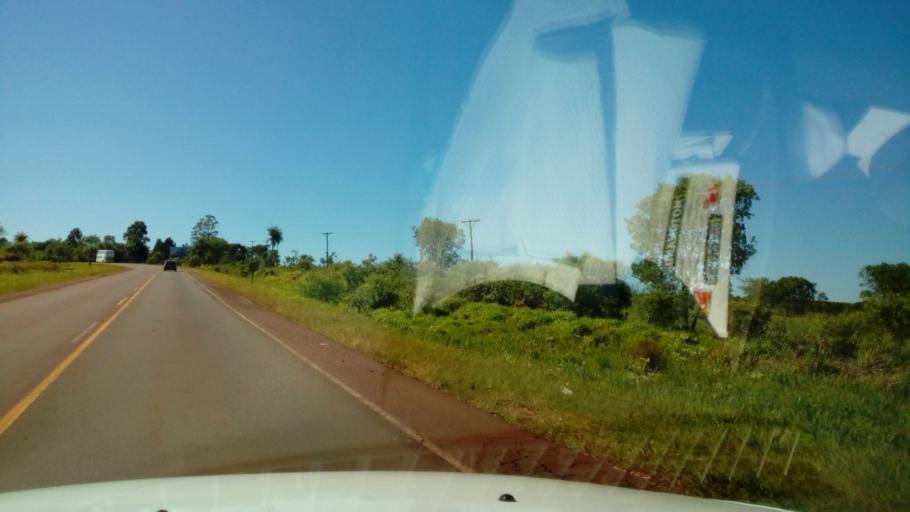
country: AR
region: Misiones
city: Santa Ana
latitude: -27.4087
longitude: -55.5521
